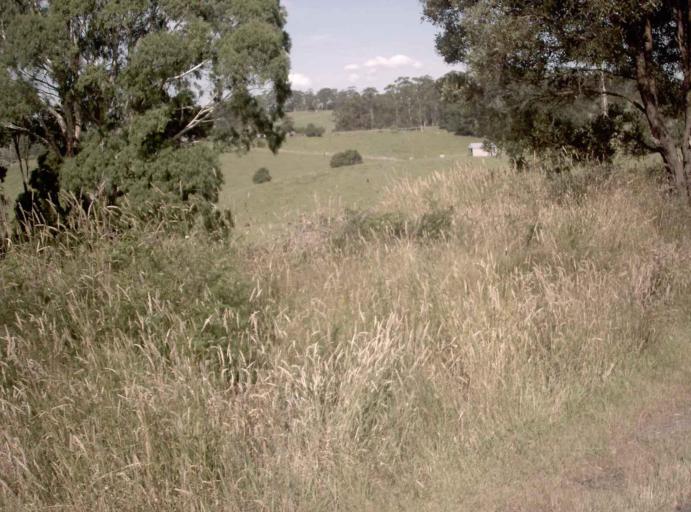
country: AU
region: Victoria
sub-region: Baw Baw
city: Warragul
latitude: -38.3574
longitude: 145.8040
